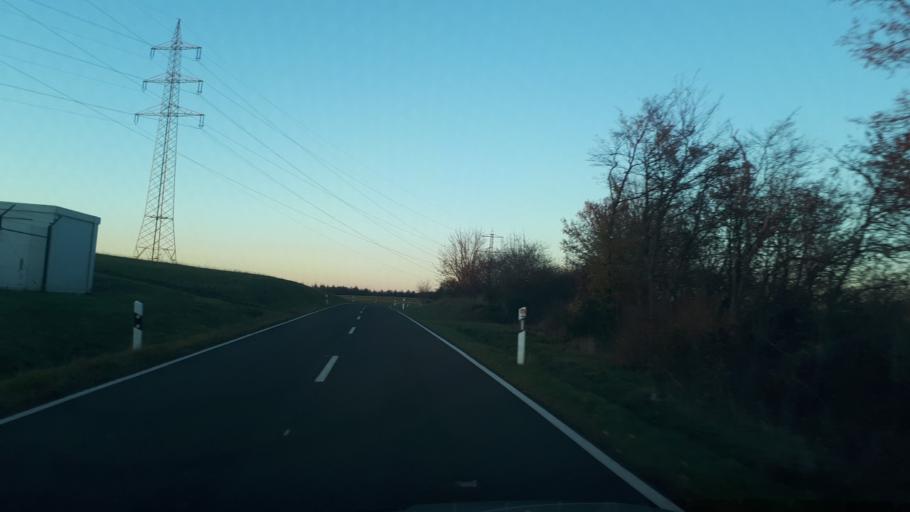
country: DE
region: Rheinland-Pfalz
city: Beuren
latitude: 50.0831
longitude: 7.0746
